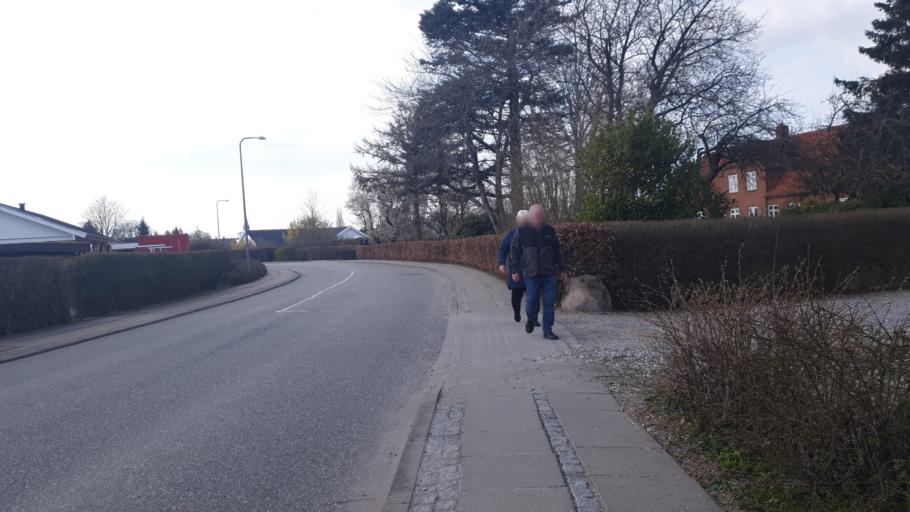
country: DK
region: Central Jutland
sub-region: Hedensted Kommune
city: Hedensted
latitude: 55.7669
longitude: 9.7101
